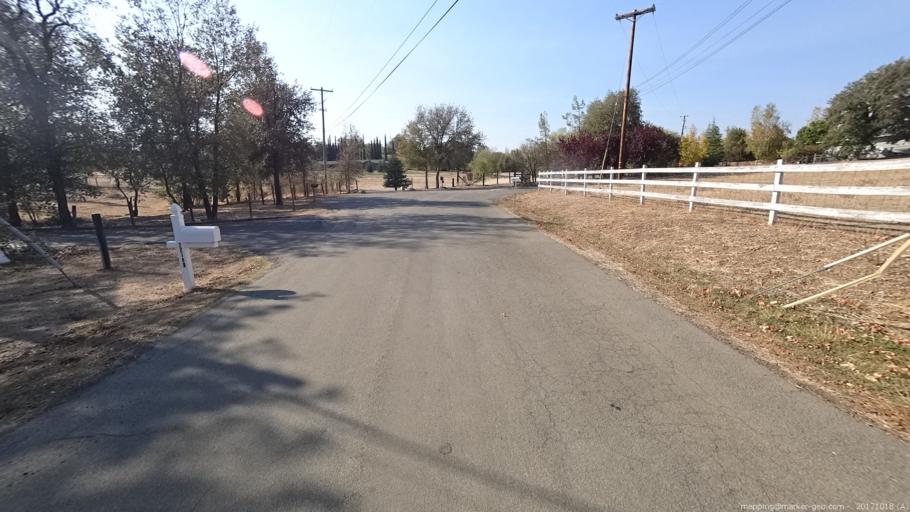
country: US
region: California
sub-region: Shasta County
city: Palo Cedro
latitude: 40.5770
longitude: -122.2315
